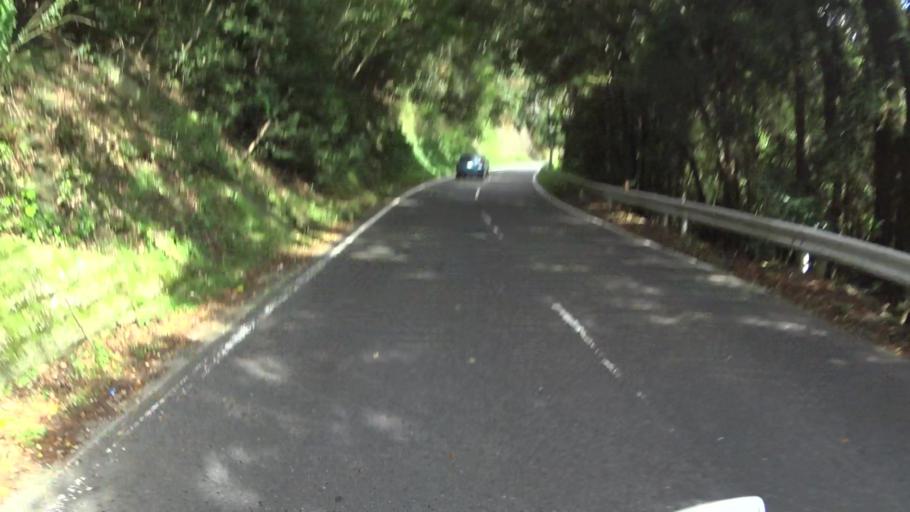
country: JP
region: Kyoto
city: Uji
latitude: 34.9186
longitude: 135.8588
